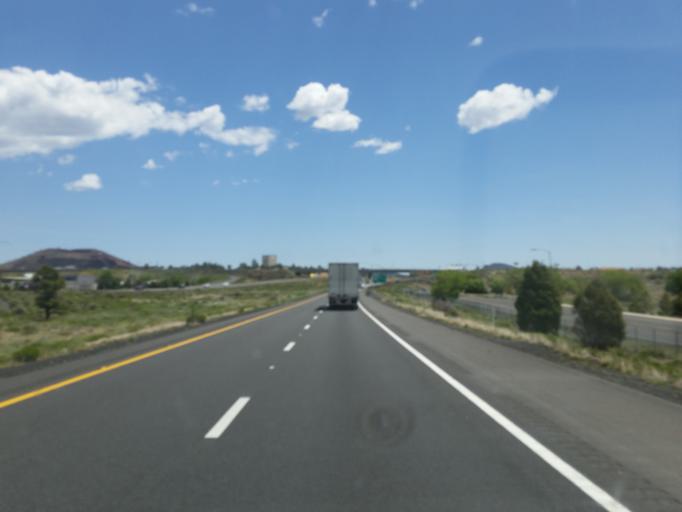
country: US
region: Arizona
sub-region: Coconino County
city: Flagstaff
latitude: 35.2141
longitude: -111.5889
